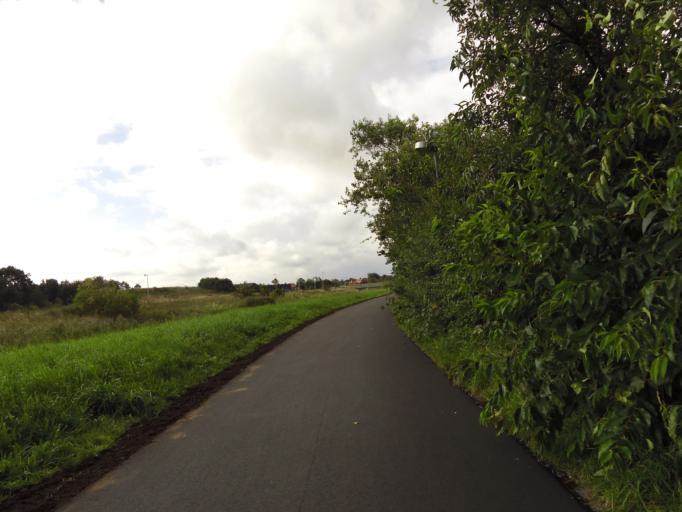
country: DK
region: South Denmark
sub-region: Esbjerg Kommune
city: Ribe
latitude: 55.3356
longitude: 8.7802
